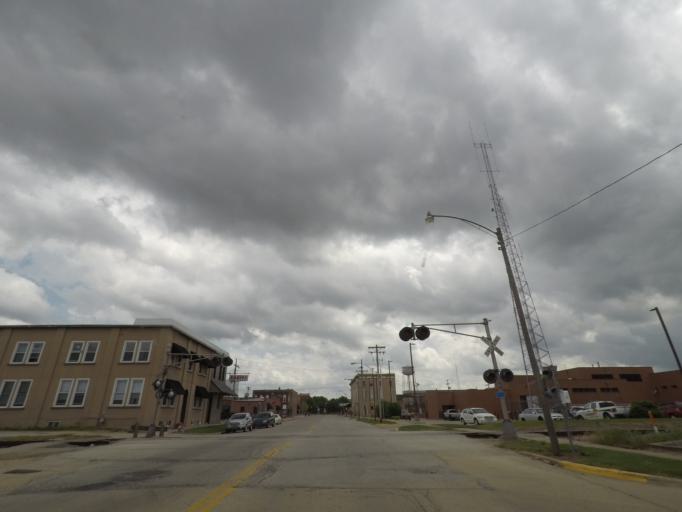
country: US
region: Illinois
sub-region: De Witt County
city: Clinton
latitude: 40.1547
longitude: -88.9606
